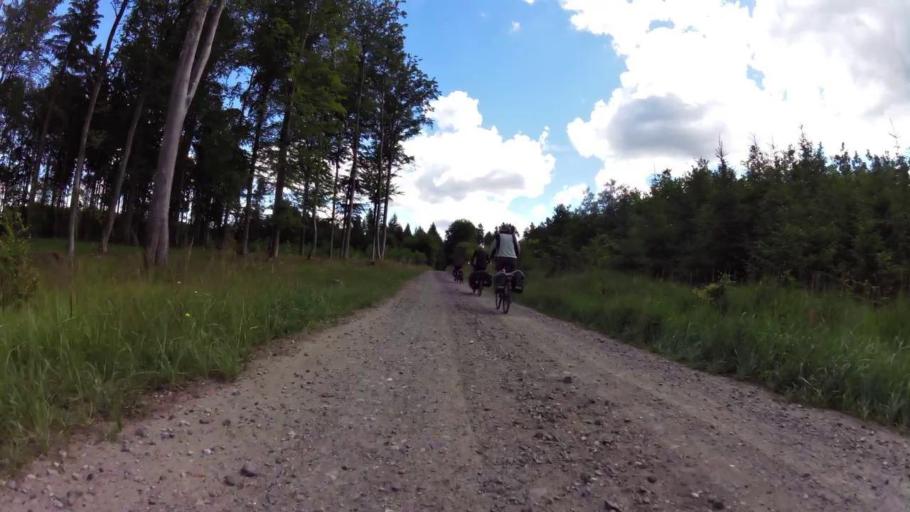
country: PL
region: West Pomeranian Voivodeship
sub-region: Powiat lobeski
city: Radowo Male
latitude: 53.7347
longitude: 15.5232
